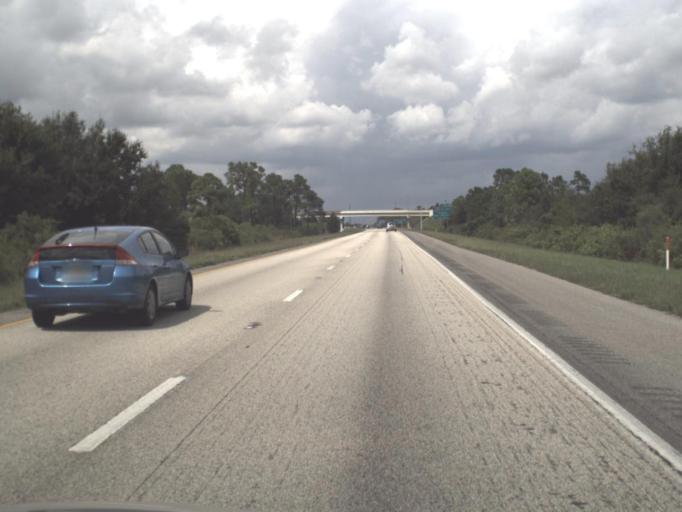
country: US
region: Florida
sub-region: Charlotte County
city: Harbour Heights
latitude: 26.9994
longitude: -82.0351
